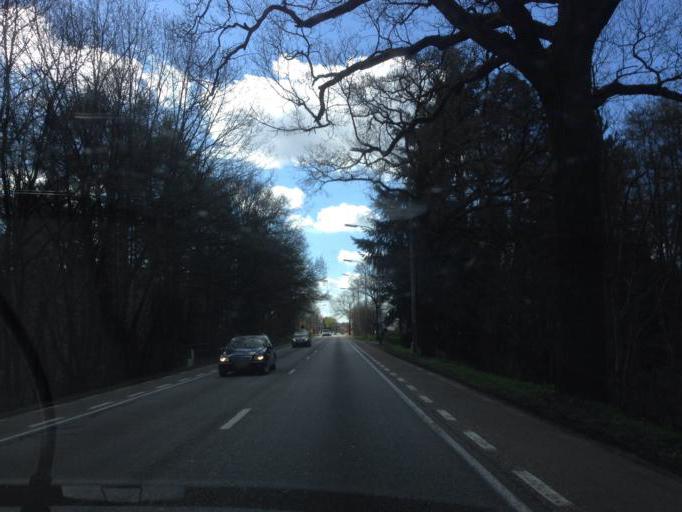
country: BE
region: Flanders
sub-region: Provincie Limburg
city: Helchteren
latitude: 51.0668
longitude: 5.3823
